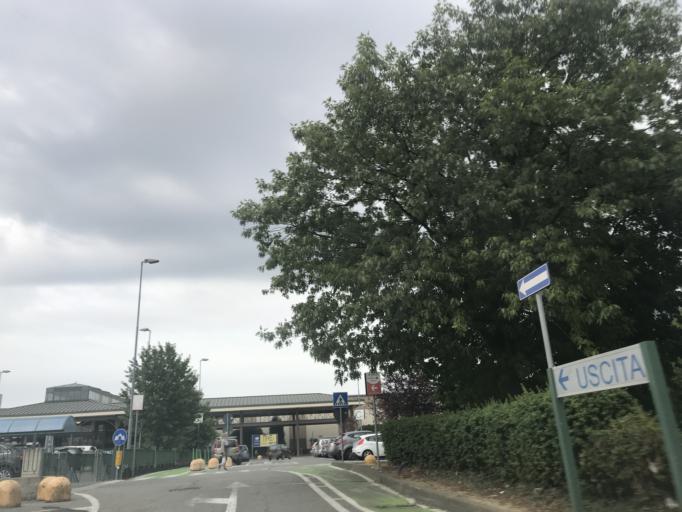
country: IT
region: Lombardy
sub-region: Citta metropolitana di Milano
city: Rozzano
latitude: 45.4034
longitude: 9.1503
